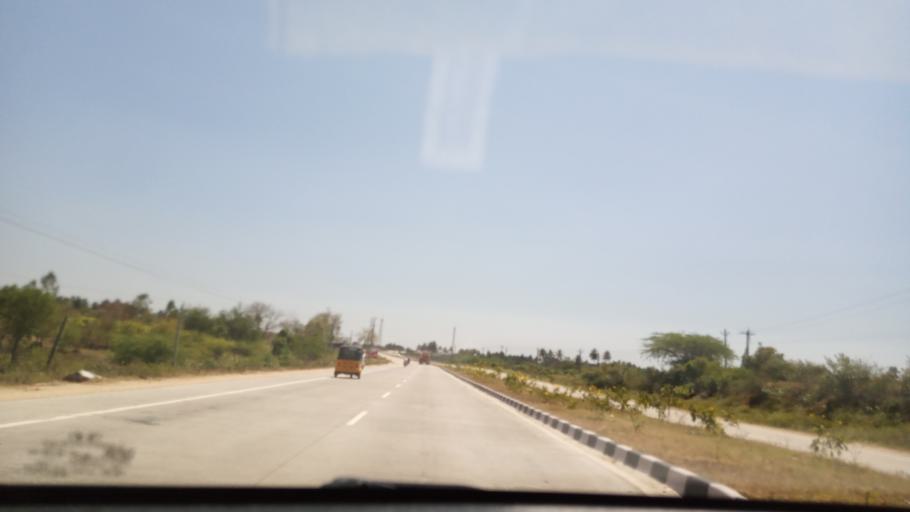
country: IN
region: Andhra Pradesh
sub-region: Chittoor
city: Chittoor
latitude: 13.2028
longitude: 78.9495
